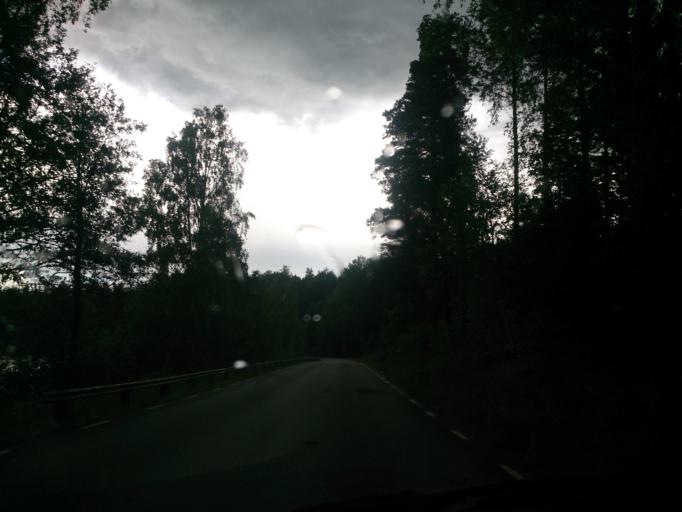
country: SE
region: OEstergoetland
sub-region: Norrkopings Kommun
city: Norrkoping
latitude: 58.4374
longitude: 16.1521
